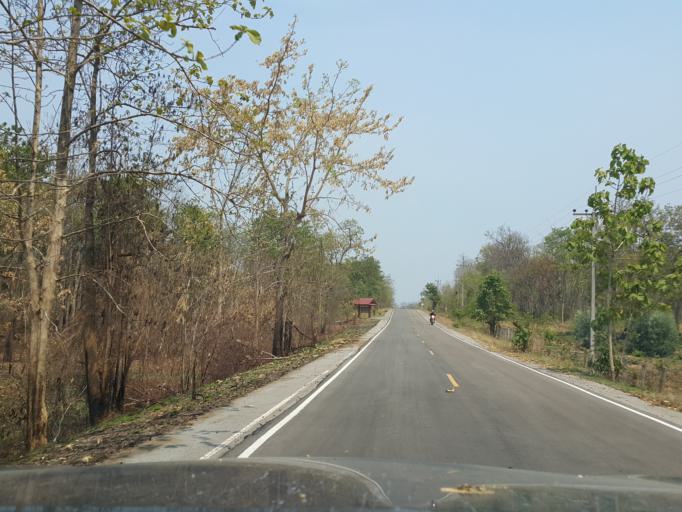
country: TH
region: Lampang
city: Mae Phrik
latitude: 17.5590
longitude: 99.1000
